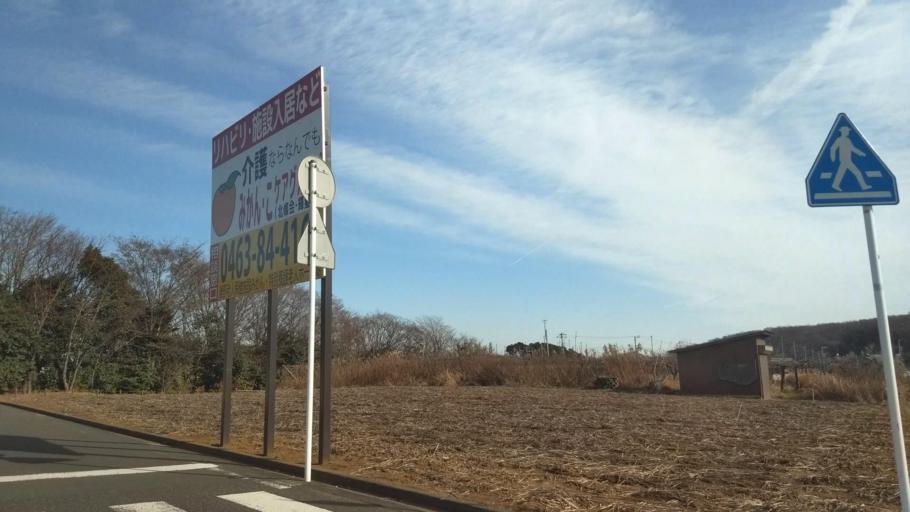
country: JP
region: Kanagawa
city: Hadano
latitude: 35.3602
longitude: 139.2305
